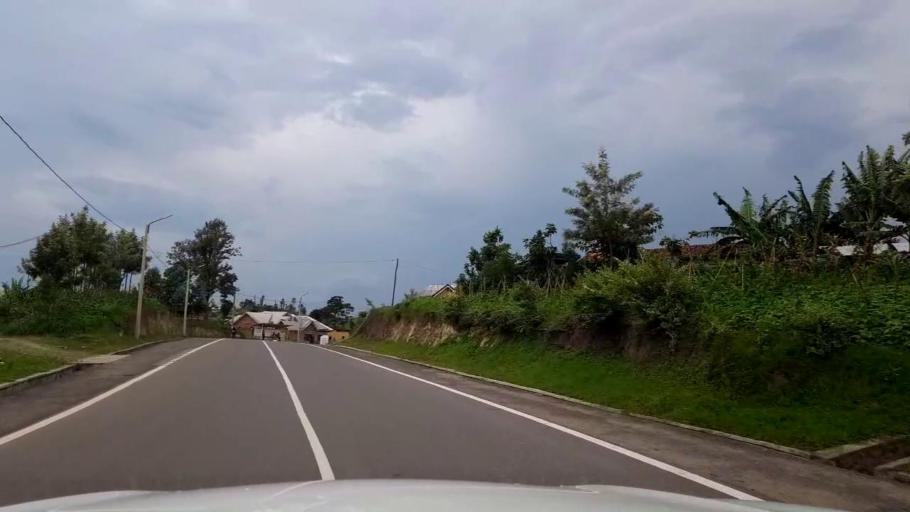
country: RW
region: Western Province
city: Kibuye
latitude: -2.0427
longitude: 29.4065
